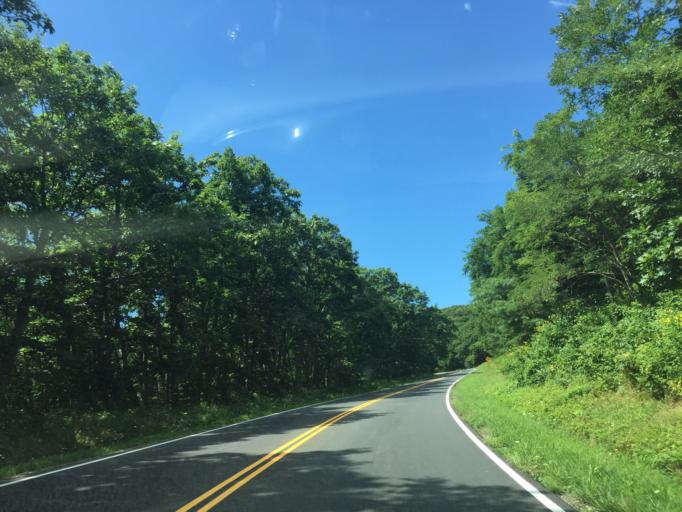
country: US
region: Virginia
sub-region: Rappahannock County
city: Washington
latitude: 38.7570
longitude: -78.2710
